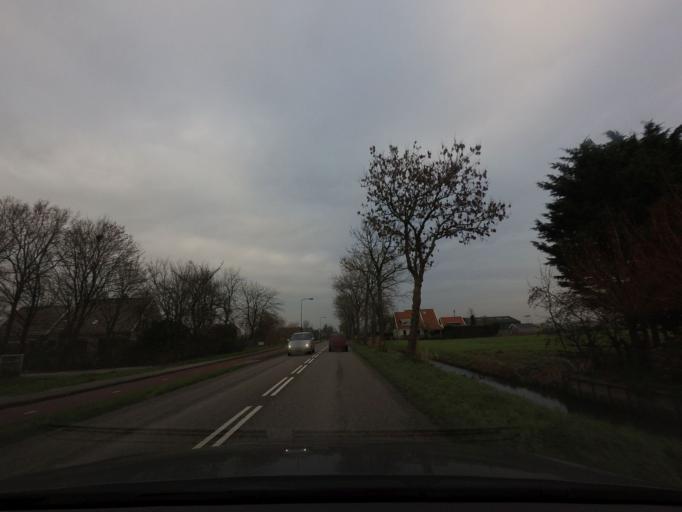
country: NL
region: North Holland
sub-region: Gemeente Heerhugowaard
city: Heerhugowaard
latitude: 52.7008
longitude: 4.8513
